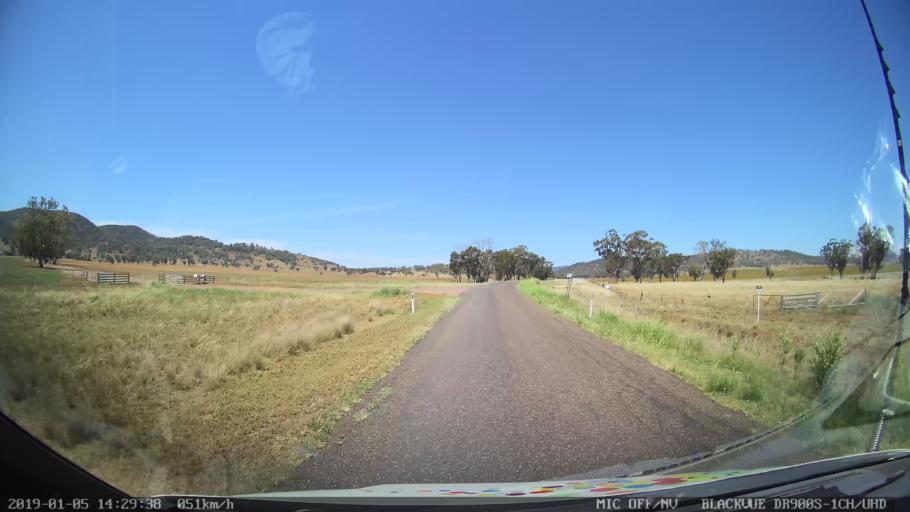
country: AU
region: New South Wales
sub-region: Tamworth Municipality
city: Phillip
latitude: -31.2284
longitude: 150.5832
